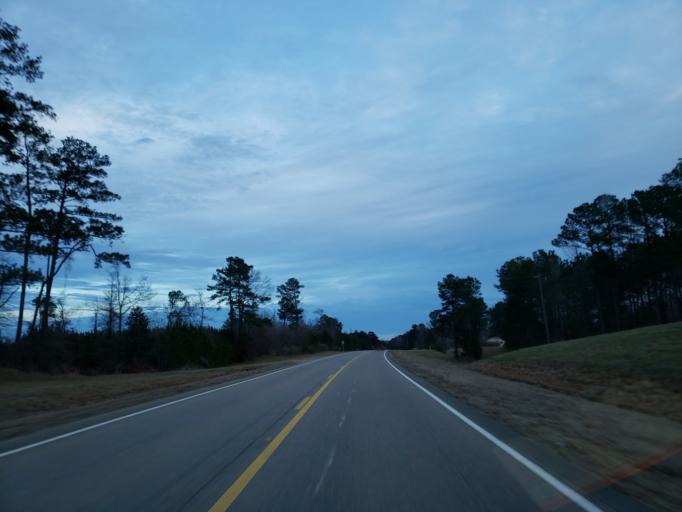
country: US
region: Mississippi
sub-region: Kemper County
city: De Kalb
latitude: 32.8310
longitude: -88.3650
